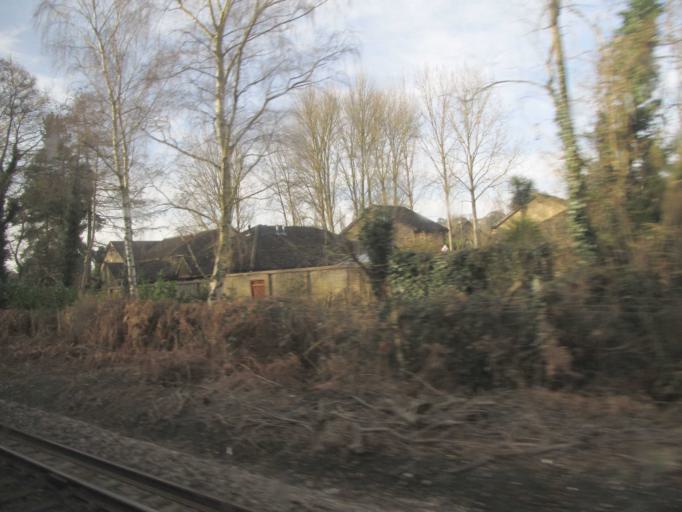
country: GB
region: England
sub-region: Surrey
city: Frimley
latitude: 51.3048
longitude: -0.7444
